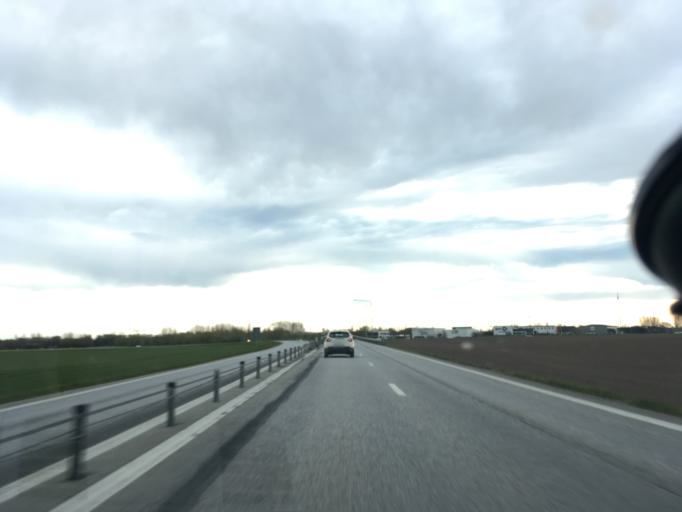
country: SE
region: Skane
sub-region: Vellinge Kommun
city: Vellinge
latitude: 55.4563
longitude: 13.0091
